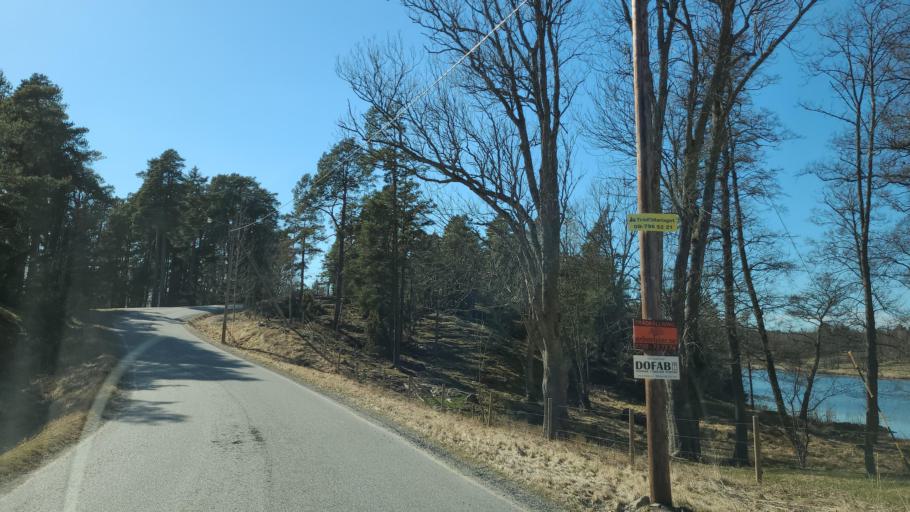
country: SE
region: Stockholm
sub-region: Varmdo Kommun
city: Hemmesta
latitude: 59.2781
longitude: 18.5633
